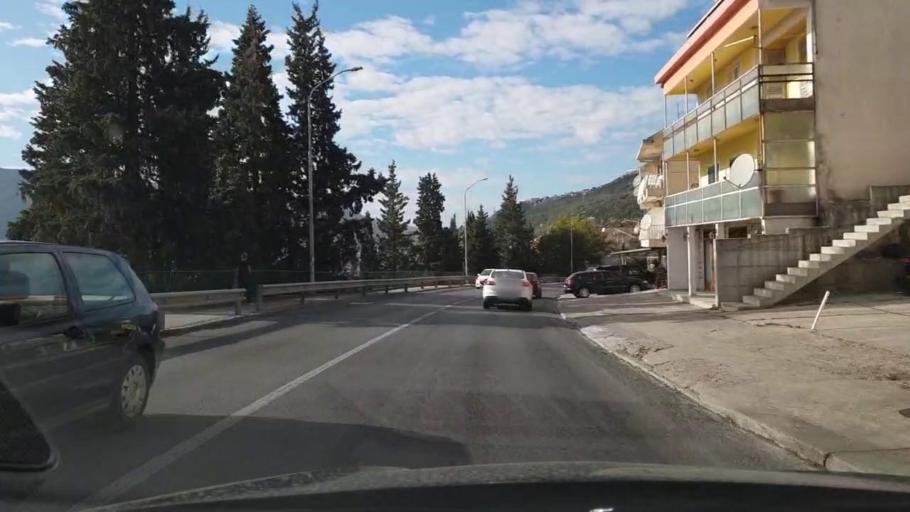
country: ME
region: Herceg Novi
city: Herceg-Novi
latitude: 42.4557
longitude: 18.5281
